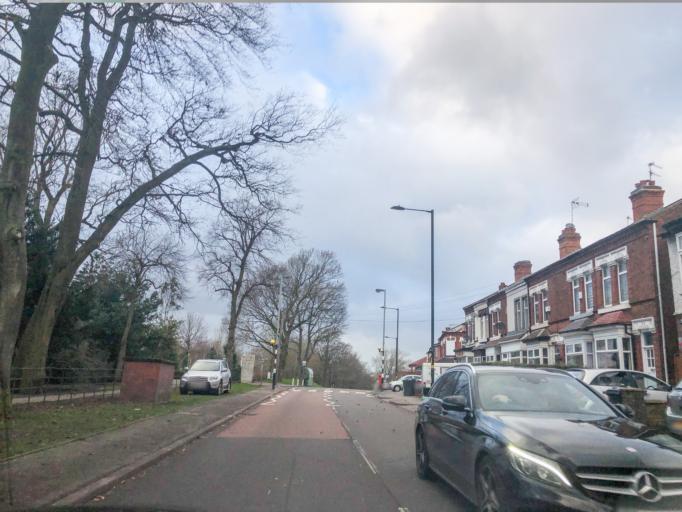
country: GB
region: England
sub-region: City and Borough of Birmingham
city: Birmingham
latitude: 52.4329
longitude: -1.9000
